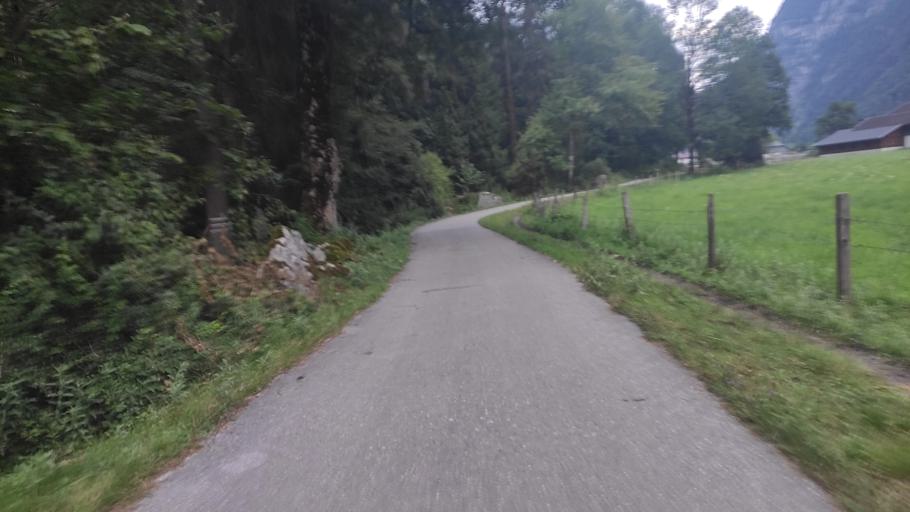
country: AT
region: Salzburg
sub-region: Politischer Bezirk Zell am See
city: Leogang
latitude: 47.4994
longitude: 12.7937
